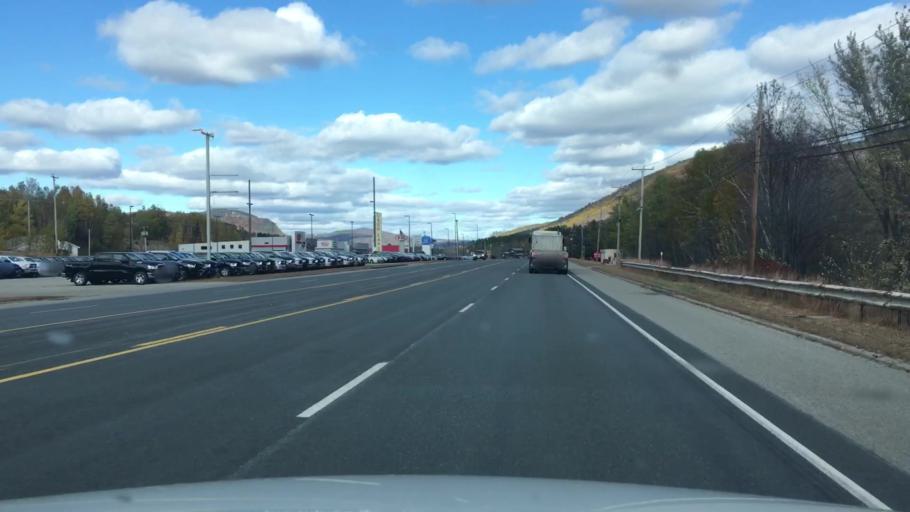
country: US
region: New Hampshire
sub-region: Coos County
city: Gorham
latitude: 44.4110
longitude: -71.1956
